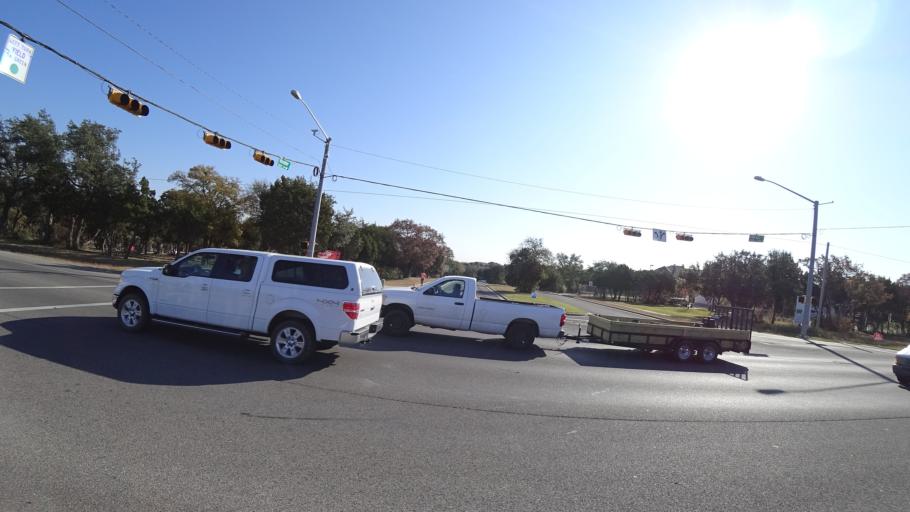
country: US
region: Texas
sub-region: Williamson County
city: Anderson Mill
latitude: 30.4289
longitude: -97.8427
